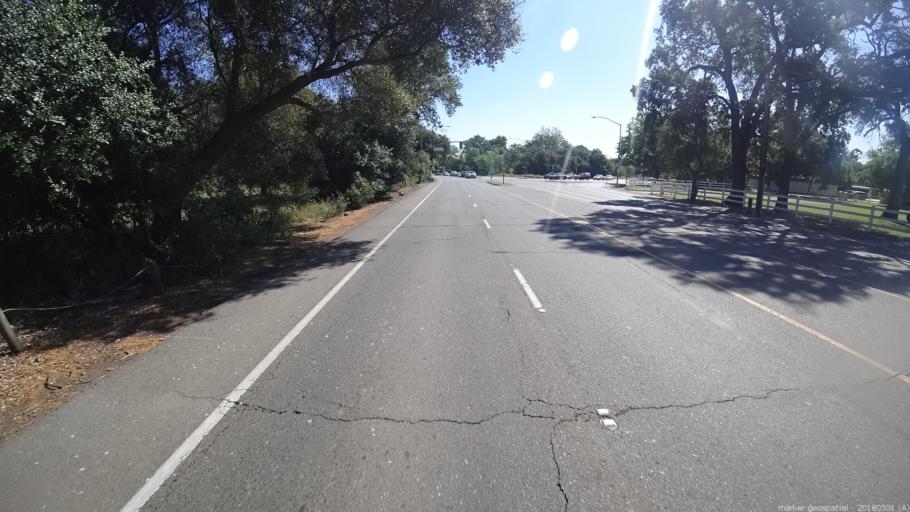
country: US
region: California
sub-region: Sacramento County
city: Foothill Farms
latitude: 38.6422
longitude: -121.3681
